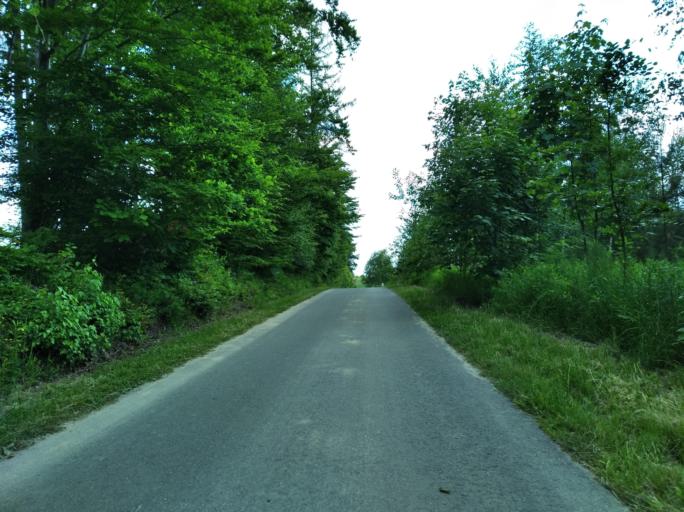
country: PL
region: Subcarpathian Voivodeship
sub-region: Powiat ropczycko-sedziszowski
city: Zagorzyce
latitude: 49.9662
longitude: 21.7127
